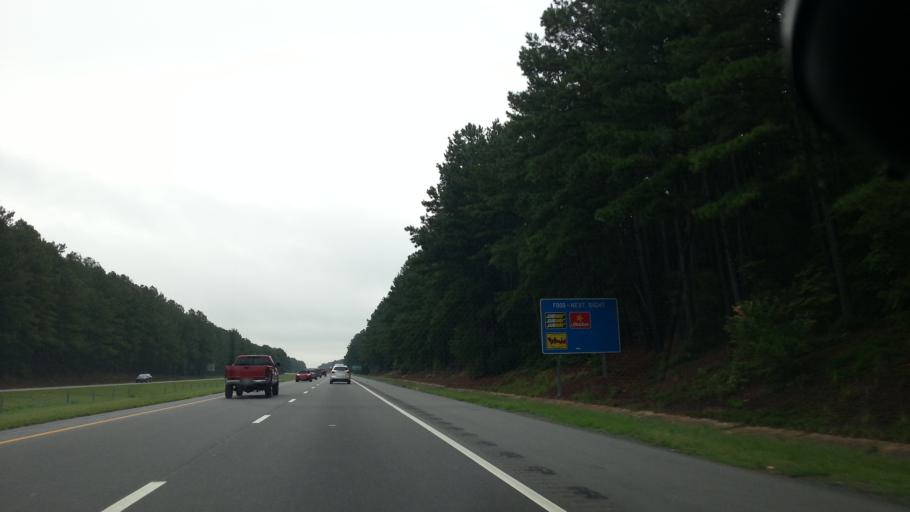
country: US
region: North Carolina
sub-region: Cumberland County
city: Fort Bragg
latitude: 35.0868
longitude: -78.9657
